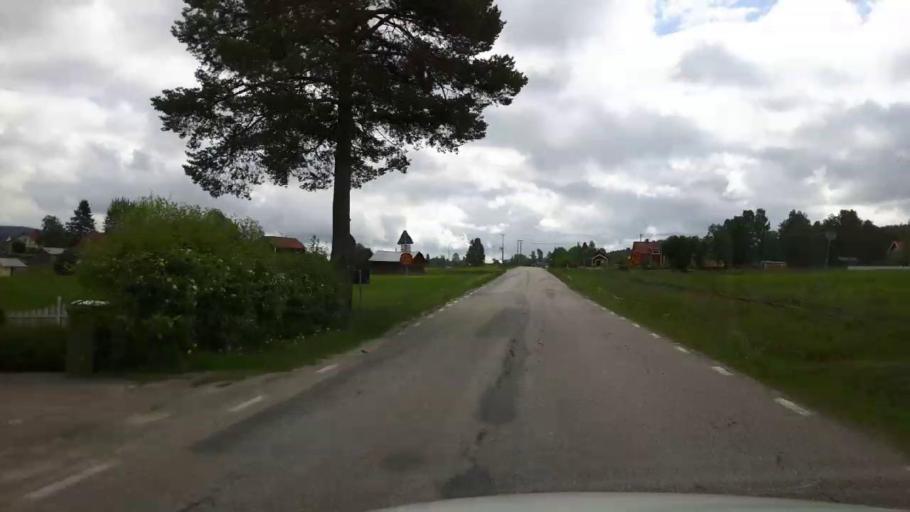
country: SE
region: Gaevleborg
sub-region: Ovanakers Kommun
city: Edsbyn
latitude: 61.3583
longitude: 15.8977
